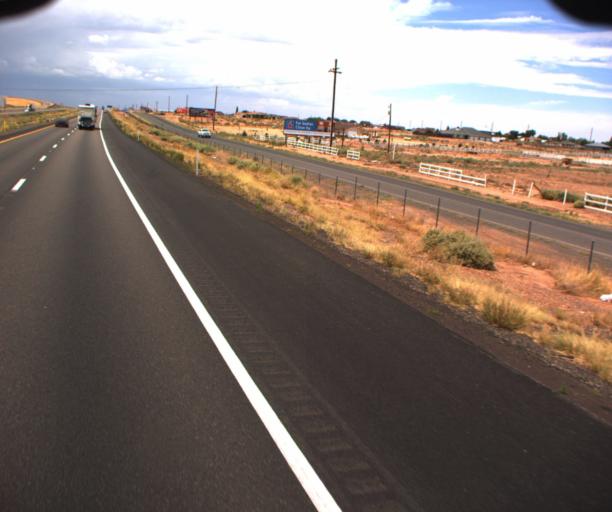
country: US
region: Arizona
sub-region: Coconino County
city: LeChee
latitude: 35.0389
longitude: -110.7338
